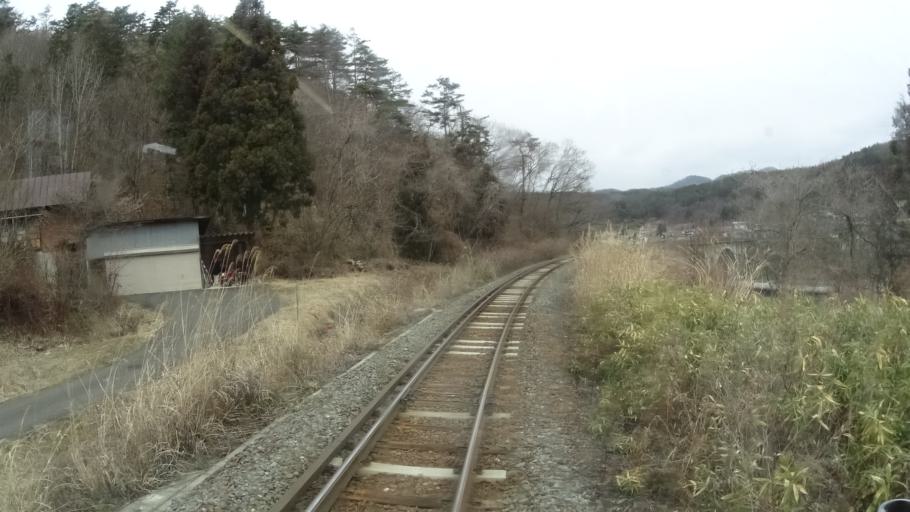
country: JP
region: Iwate
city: Tono
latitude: 39.3460
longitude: 141.3494
